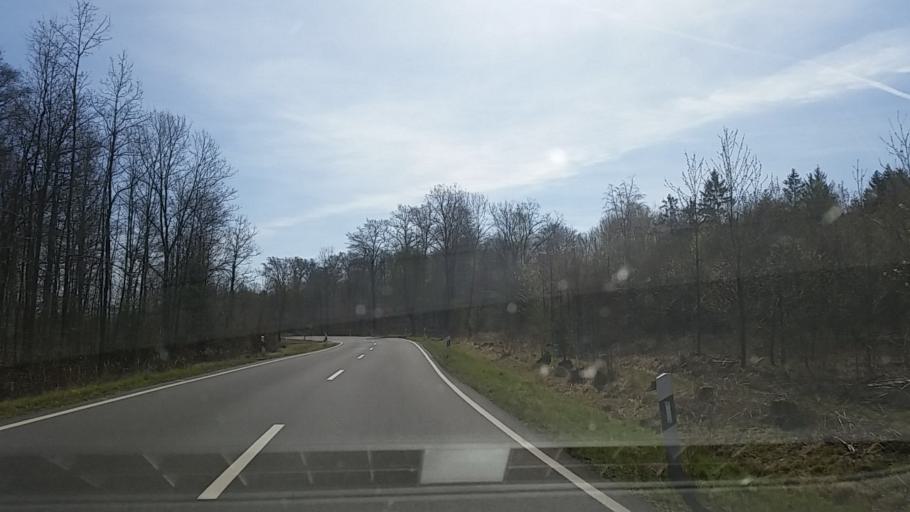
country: DE
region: Lower Saxony
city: Warberg
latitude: 52.1640
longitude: 10.8963
